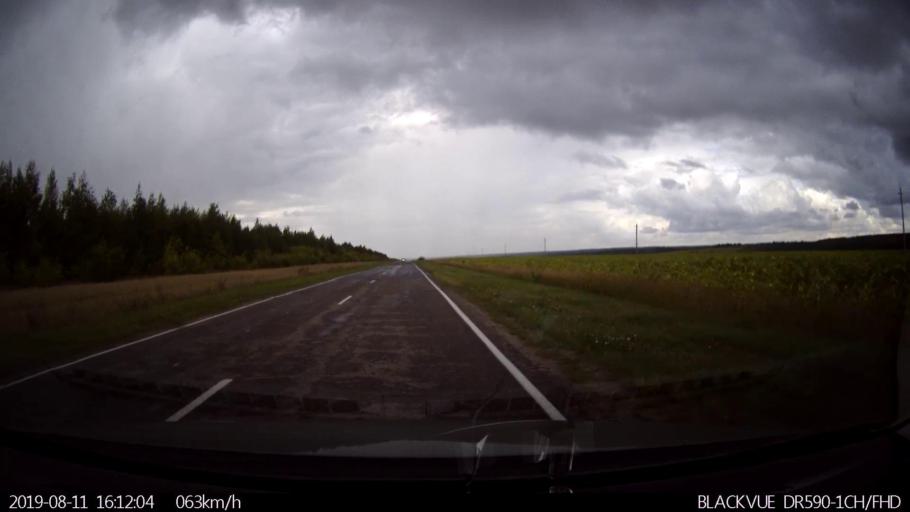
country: RU
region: Ulyanovsk
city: Ignatovka
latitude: 54.0084
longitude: 47.6416
